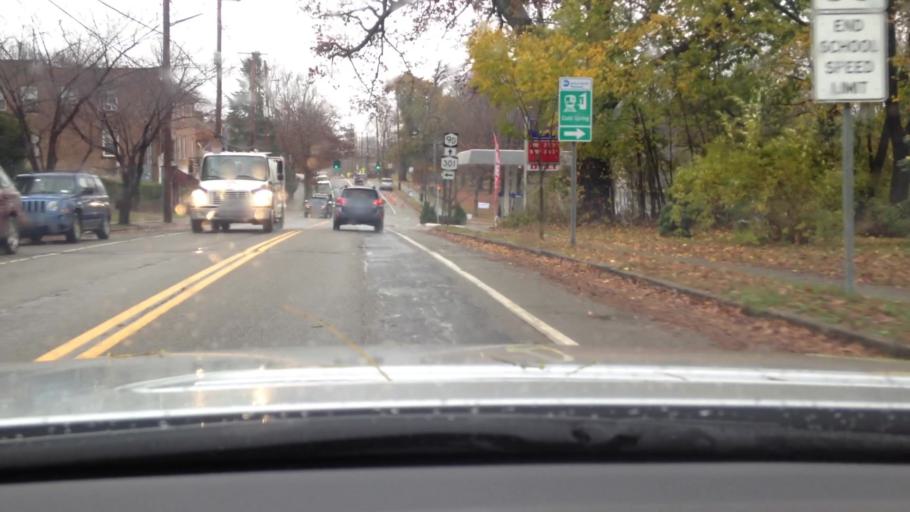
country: US
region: New York
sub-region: Putnam County
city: Cold Spring
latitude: 41.4207
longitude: -73.9557
